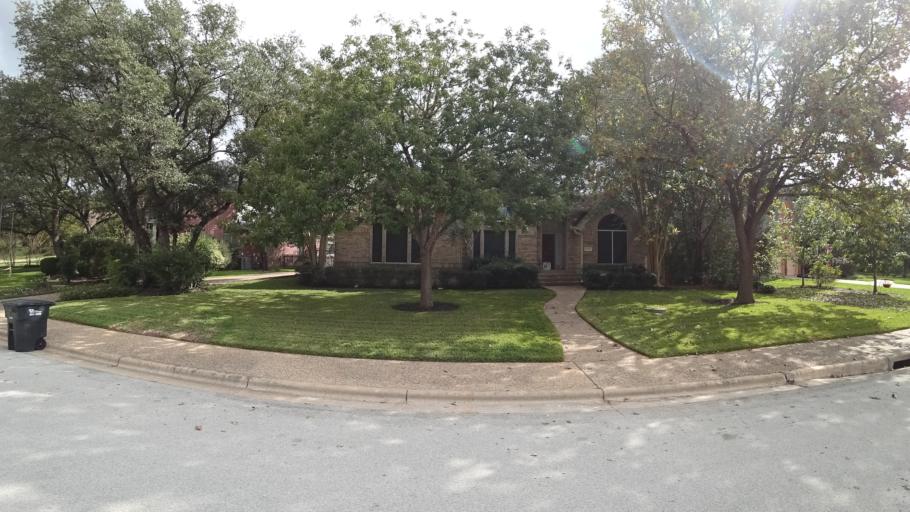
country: US
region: Texas
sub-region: Travis County
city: Barton Creek
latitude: 30.3007
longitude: -97.8953
